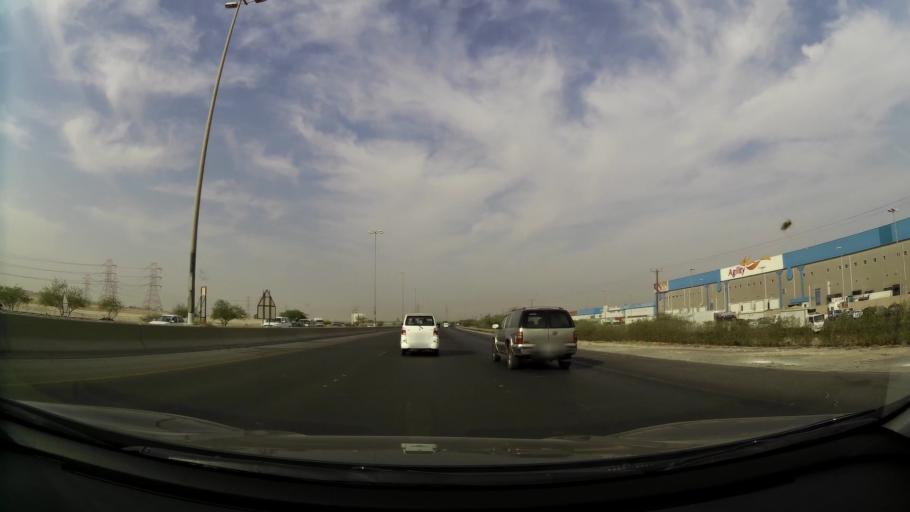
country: KW
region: Al Asimah
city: Ar Rabiyah
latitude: 29.2651
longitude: 47.8510
